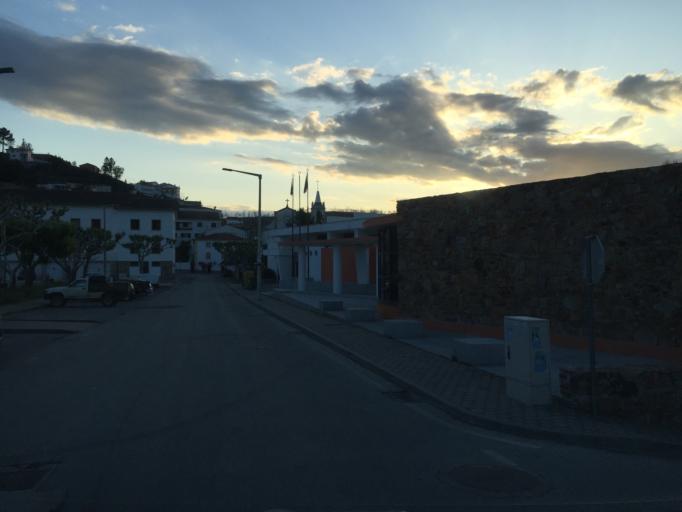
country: PT
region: Coimbra
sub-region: Pampilhosa da Serra
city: Pampilhosa da Serra
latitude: 40.0467
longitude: -7.9492
